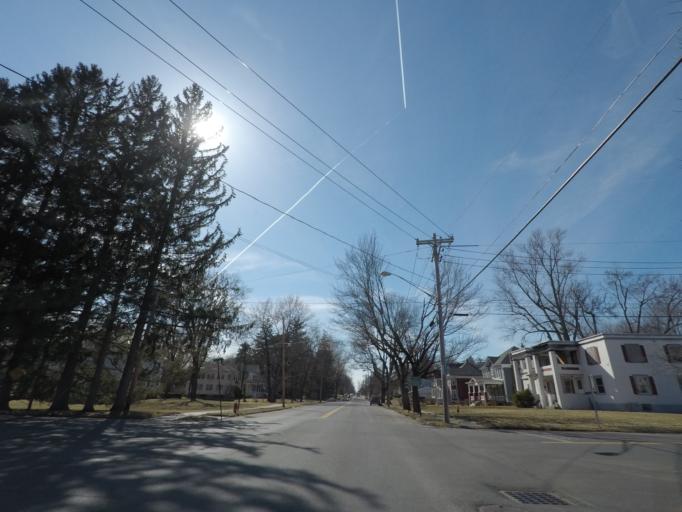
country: US
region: New York
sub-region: Saratoga County
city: Ballston Spa
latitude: 43.0013
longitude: -73.8425
